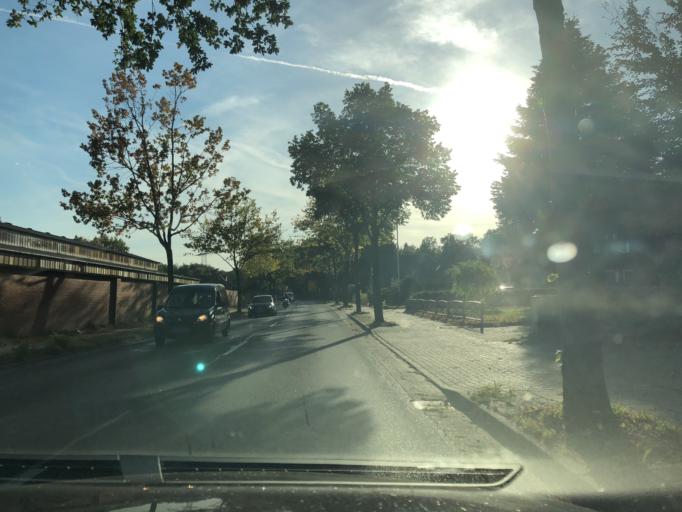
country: DE
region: Lower Saxony
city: Papenburg
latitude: 53.0661
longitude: 7.4161
